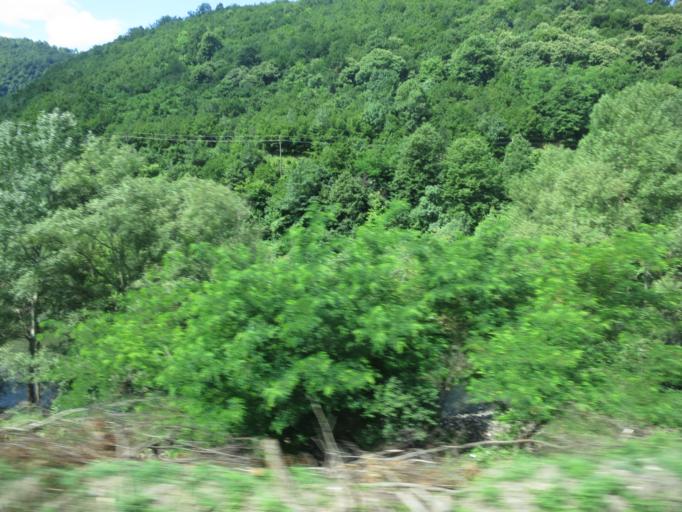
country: GE
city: Shorapani
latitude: 42.0888
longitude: 43.1423
